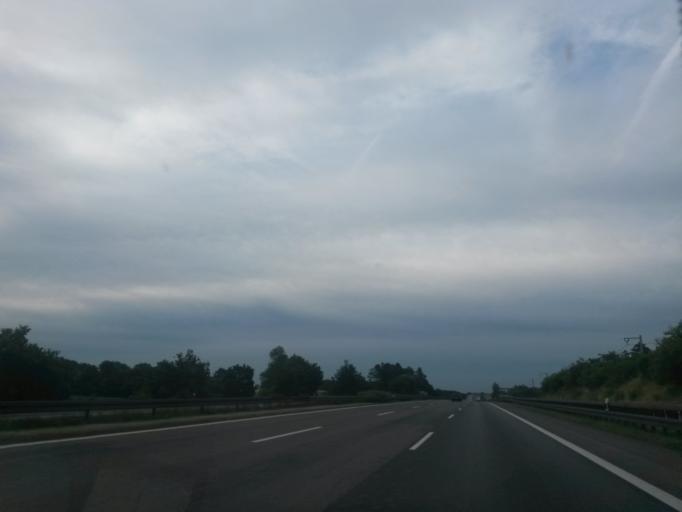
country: DE
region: Bavaria
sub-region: Regierungsbezirk Mittelfranken
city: Hilpoltstein
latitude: 49.1988
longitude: 11.2416
